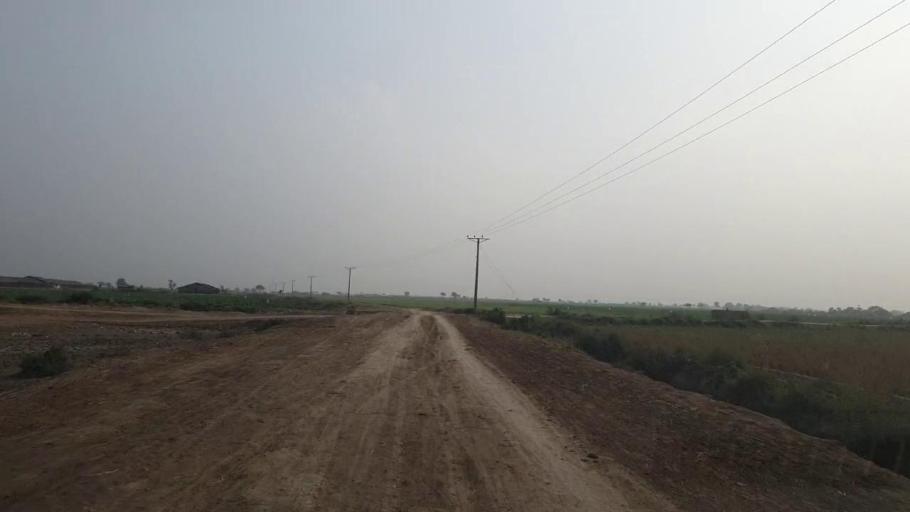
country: PK
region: Sindh
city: Mirpur Batoro
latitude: 24.5537
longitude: 68.4208
